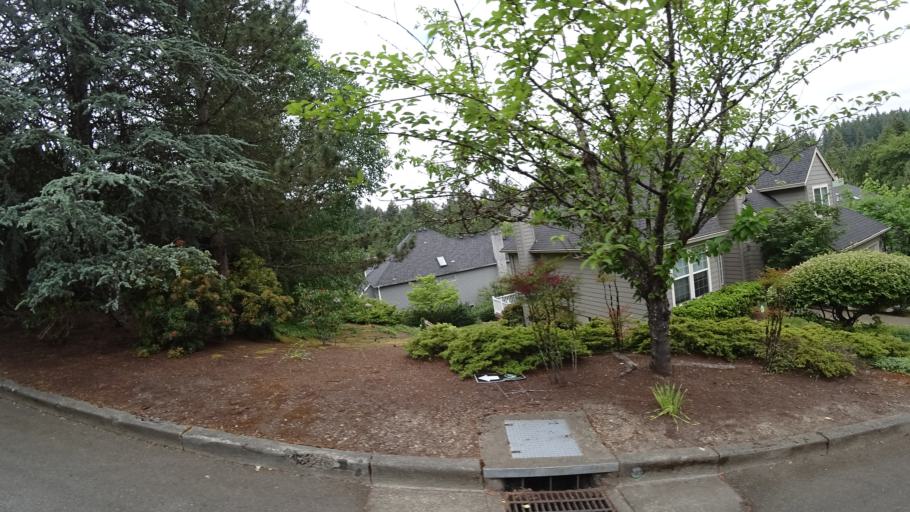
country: US
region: Oregon
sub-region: Clackamas County
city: Lake Oswego
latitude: 45.4429
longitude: -122.7048
